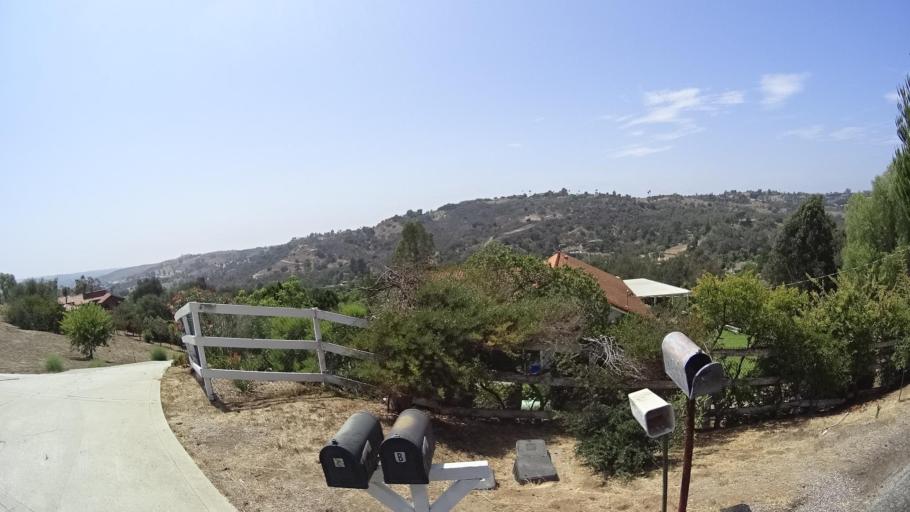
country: US
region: California
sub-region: San Diego County
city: Bonsall
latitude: 33.3127
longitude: -117.2250
